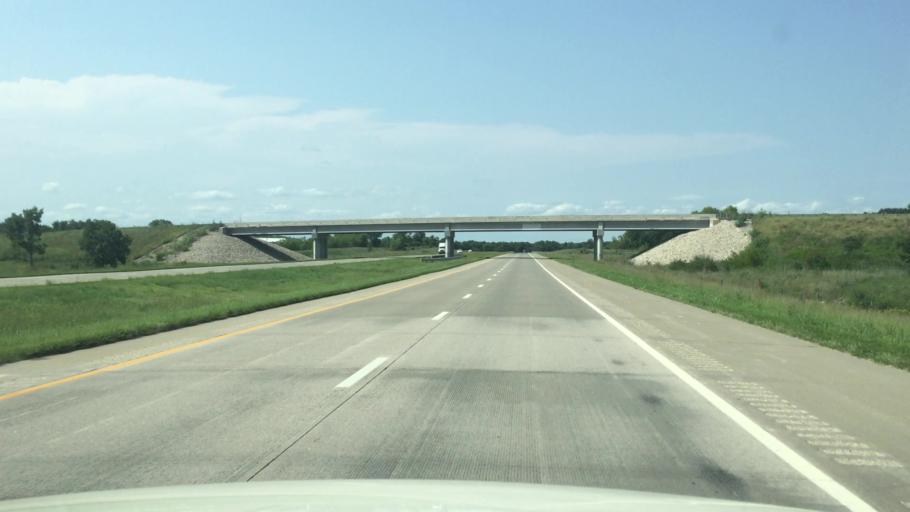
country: US
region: Kansas
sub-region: Linn County
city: La Cygne
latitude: 38.2855
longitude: -94.6728
